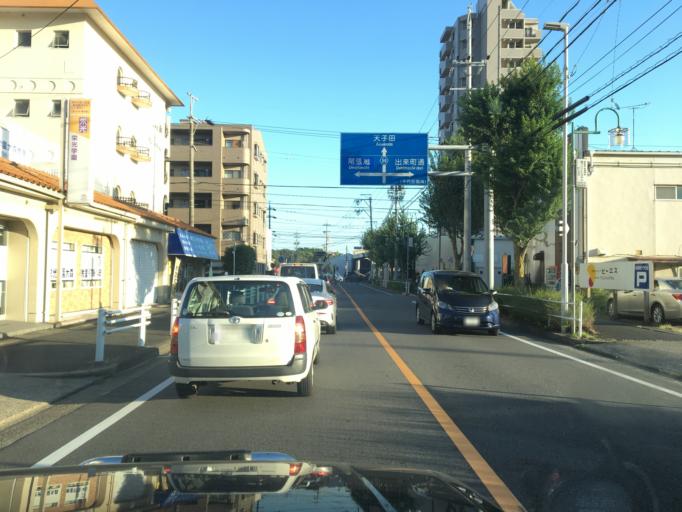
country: JP
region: Aichi
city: Kasugai
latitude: 35.2031
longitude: 136.9977
